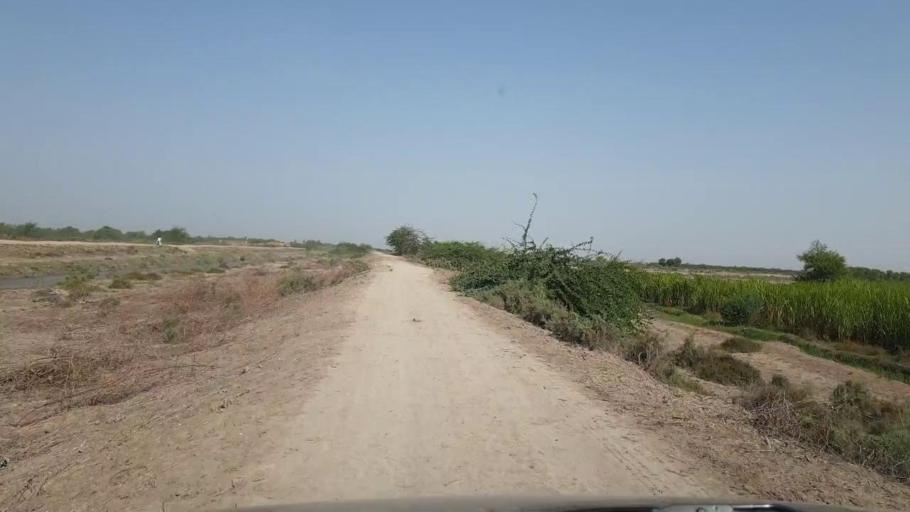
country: PK
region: Sindh
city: Kadhan
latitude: 24.6403
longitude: 69.0724
